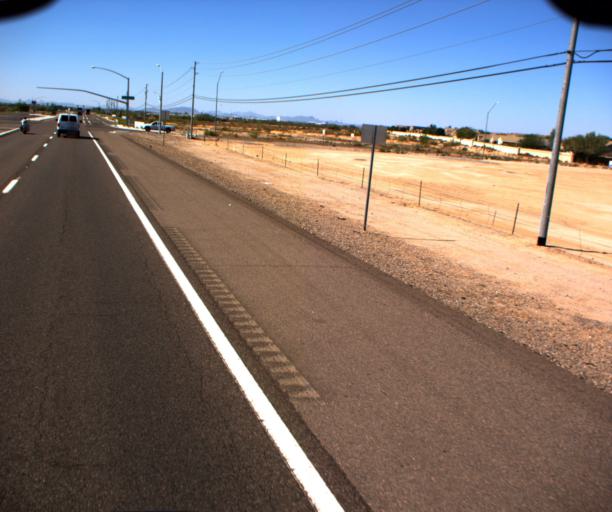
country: US
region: Arizona
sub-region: Pinal County
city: Casa Grande
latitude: 32.9721
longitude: -111.7569
